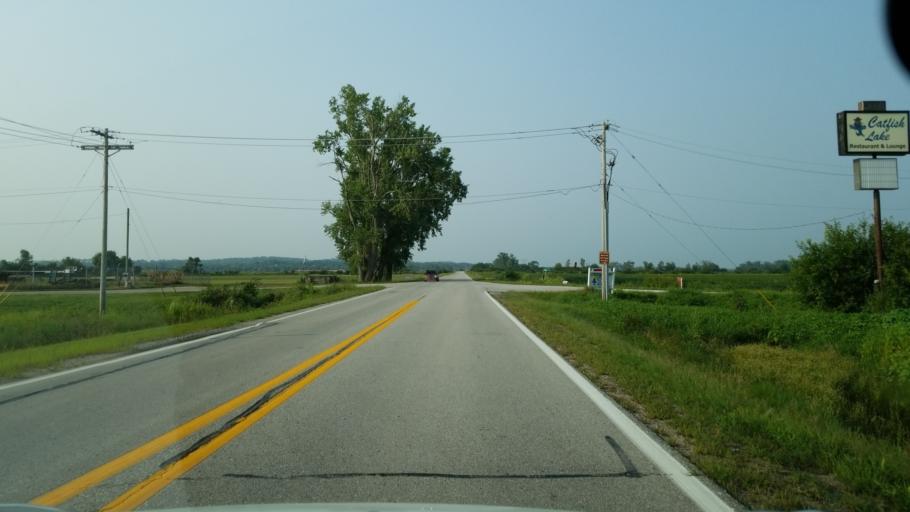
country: US
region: Nebraska
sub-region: Sarpy County
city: Bellevue
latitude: 41.1036
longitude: -95.8899
